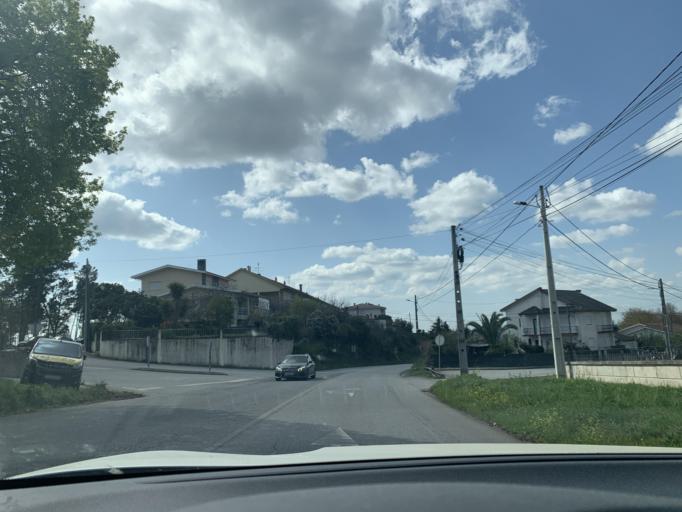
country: PT
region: Viseu
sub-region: Viseu
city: Rio de Loba
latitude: 40.6915
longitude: -7.8743
